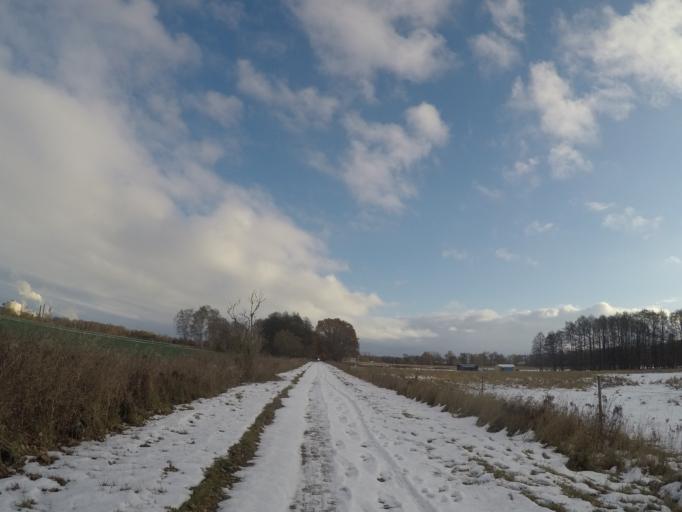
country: SE
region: Skane
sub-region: Lunds Kommun
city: Lund
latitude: 55.7818
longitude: 13.2312
